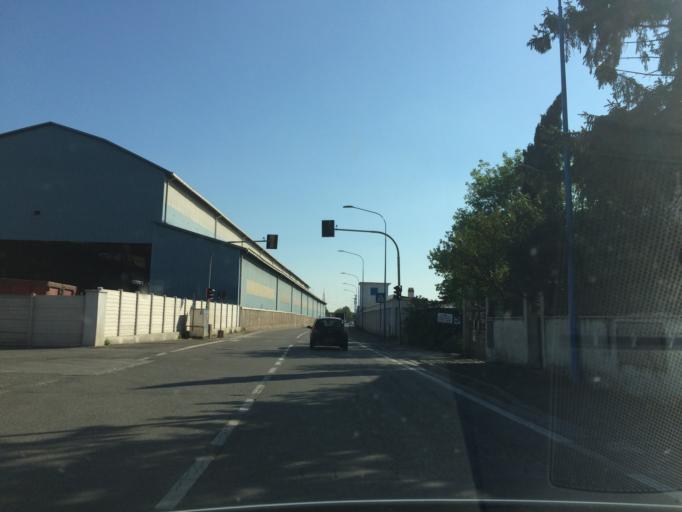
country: IT
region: Lombardy
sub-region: Provincia di Brescia
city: Folzano
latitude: 45.4959
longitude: 10.2114
